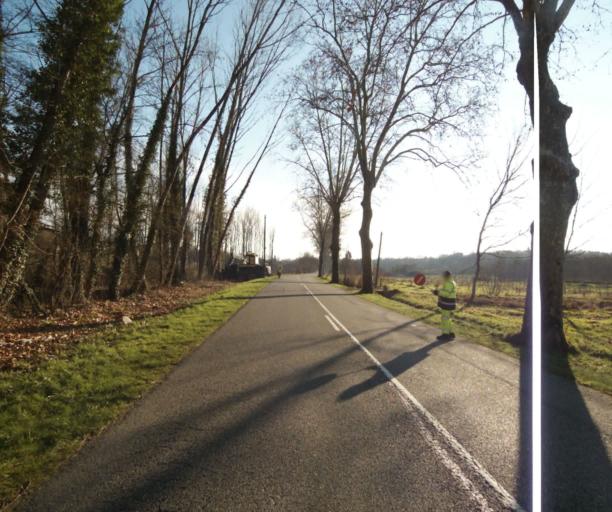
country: FR
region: Midi-Pyrenees
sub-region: Departement du Tarn-et-Garonne
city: Moissac
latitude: 44.1273
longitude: 1.1038
